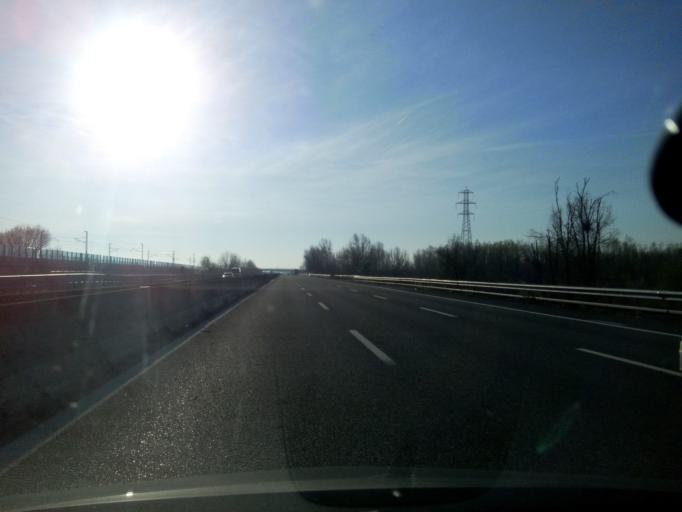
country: IT
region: Emilia-Romagna
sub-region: Provincia di Reggio Emilia
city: Praticello
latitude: 44.8064
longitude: 10.4337
